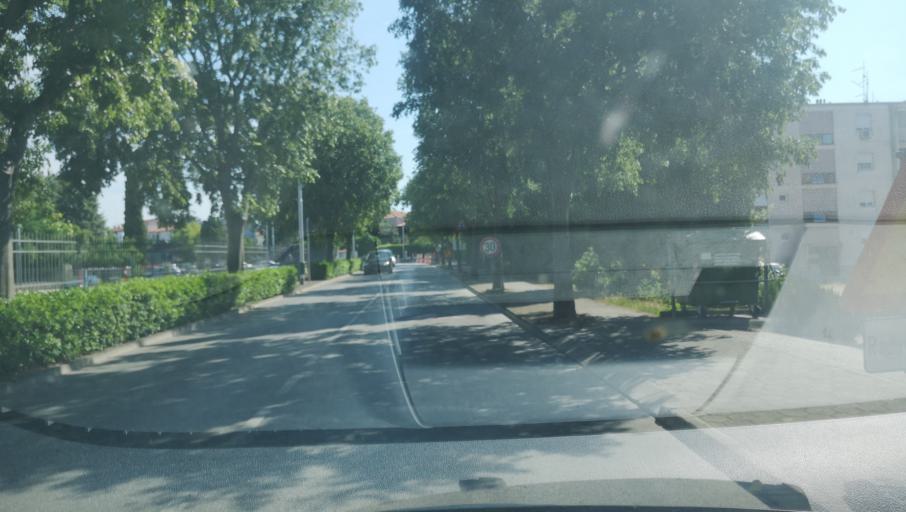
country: HR
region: Istarska
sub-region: Grad Rovinj
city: Rovinj
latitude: 45.0791
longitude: 13.6438
